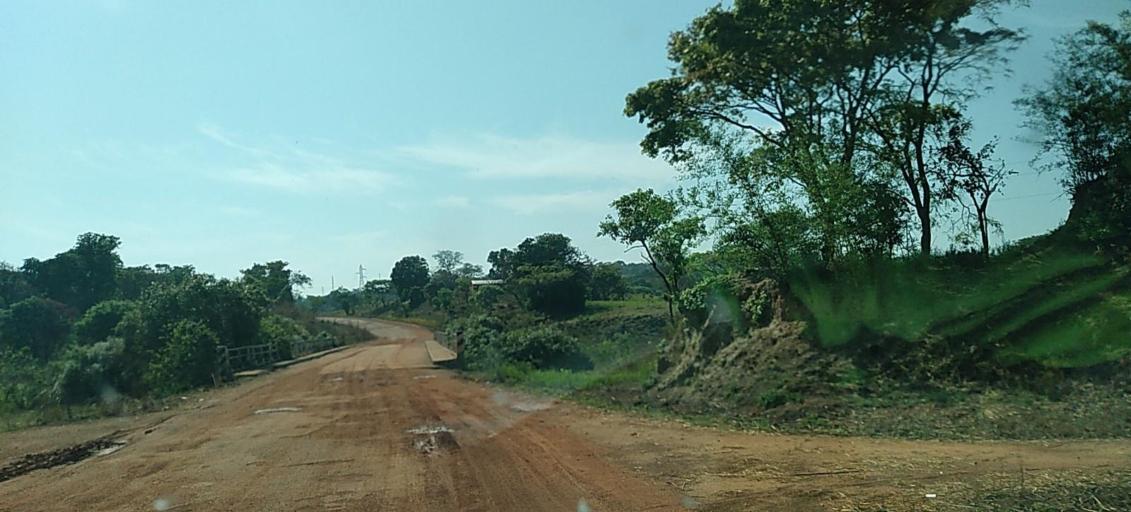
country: ZM
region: North-Western
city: Mwinilunga
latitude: -11.8253
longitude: 25.1252
